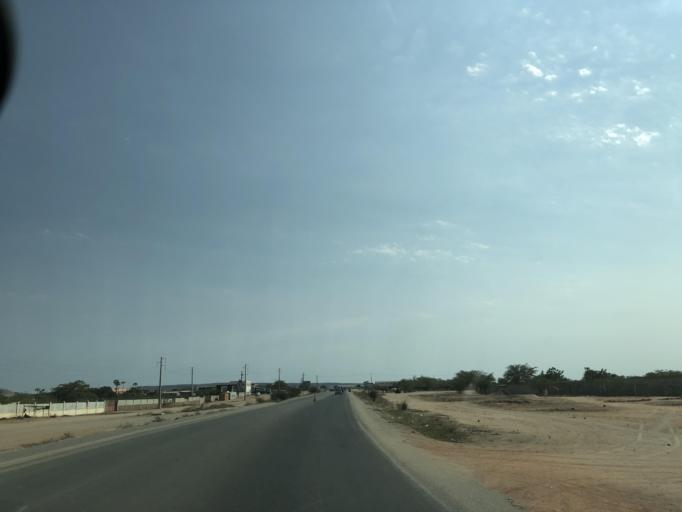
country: AO
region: Benguela
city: Benguela
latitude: -12.6414
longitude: 13.3611
